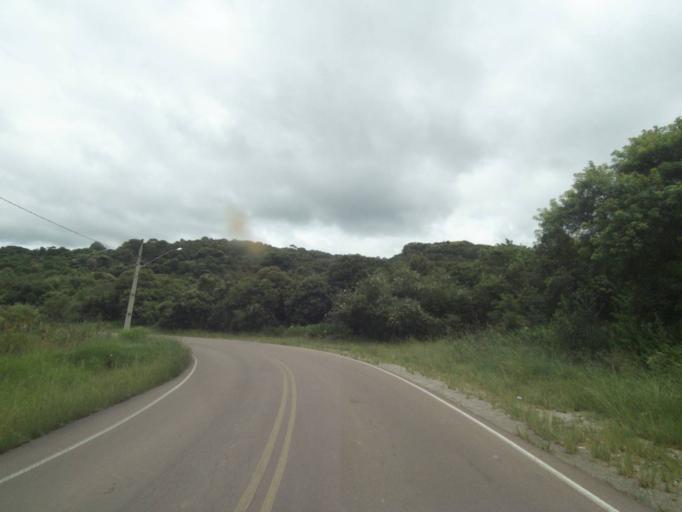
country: BR
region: Parana
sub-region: Campina Grande Do Sul
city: Campina Grande do Sul
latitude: -25.3115
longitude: -49.0182
